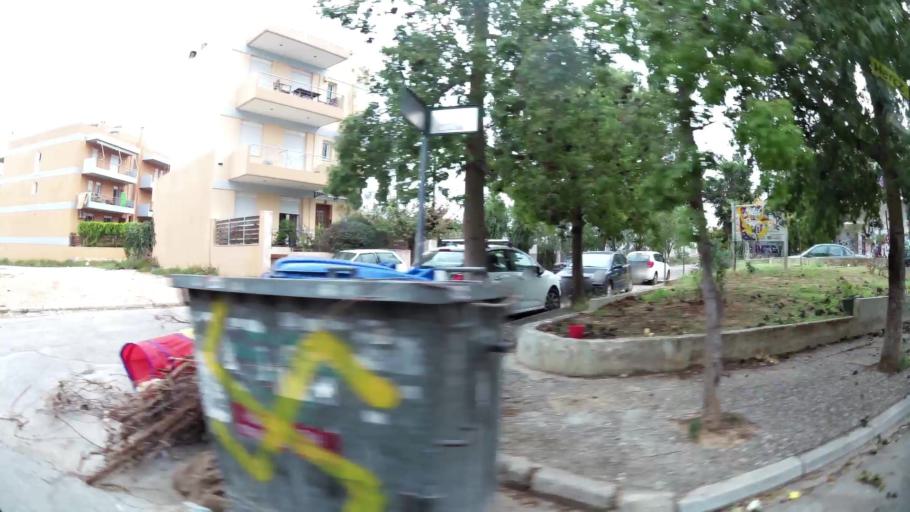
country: GR
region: Attica
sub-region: Nomarchia Athinas
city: Filothei
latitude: 38.0383
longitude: 23.7769
